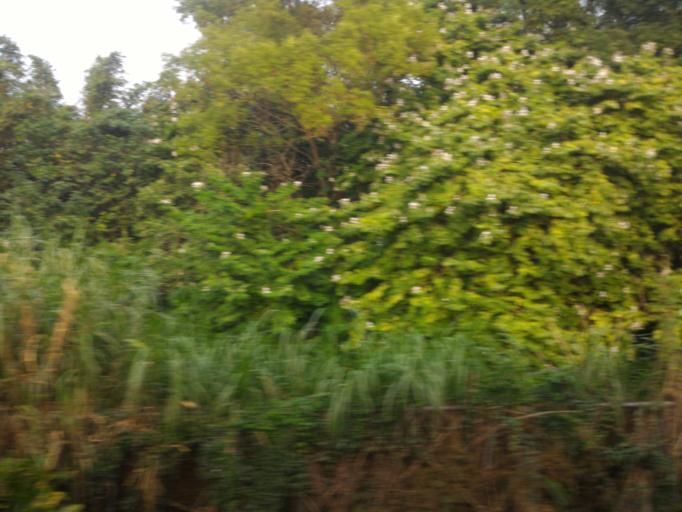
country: TW
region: Taiwan
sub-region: Taoyuan
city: Taoyuan
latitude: 24.9890
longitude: 121.3223
